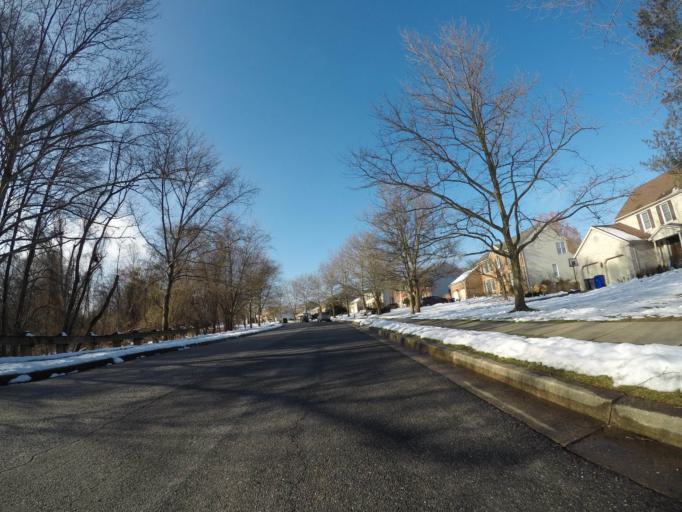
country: US
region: Maryland
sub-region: Howard County
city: Ilchester
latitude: 39.2178
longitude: -76.7839
